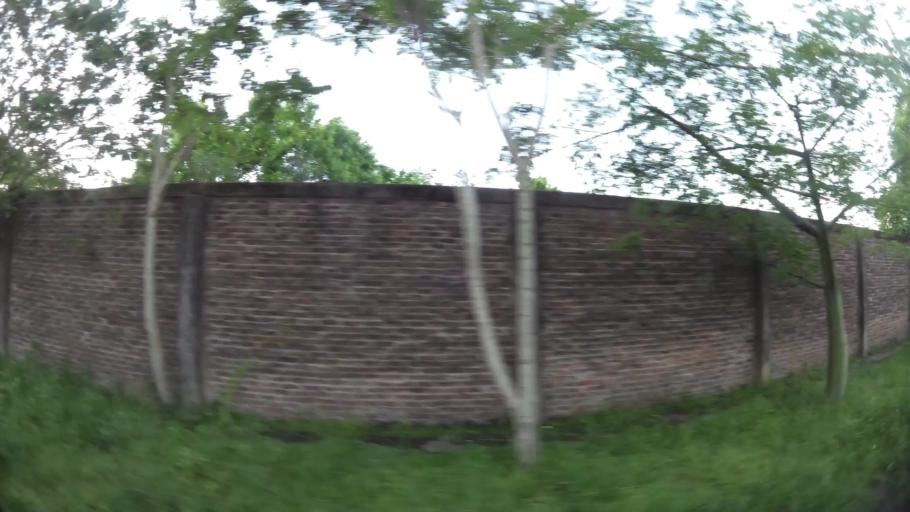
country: AR
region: Buenos Aires
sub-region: Partido de Almirante Brown
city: Adrogue
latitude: -34.7965
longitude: -58.3427
